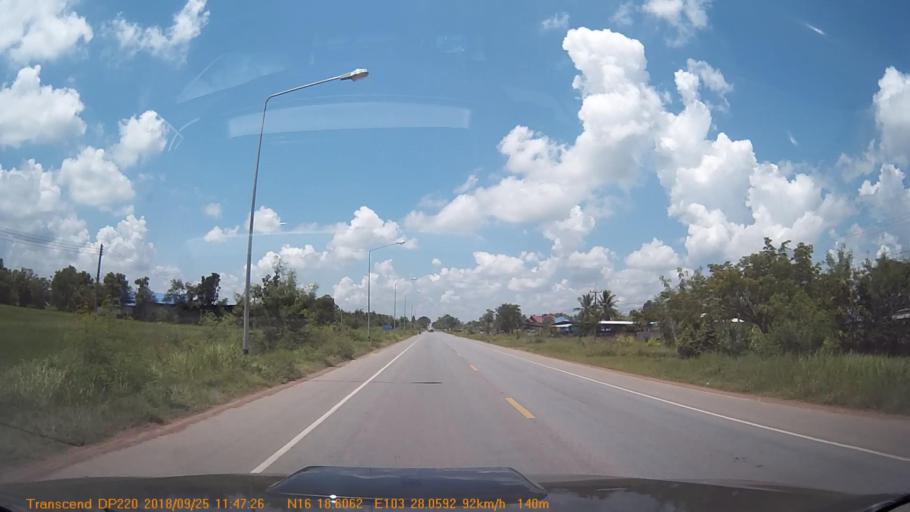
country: TH
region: Kalasin
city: Khong Chai
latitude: 16.3100
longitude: 103.4678
